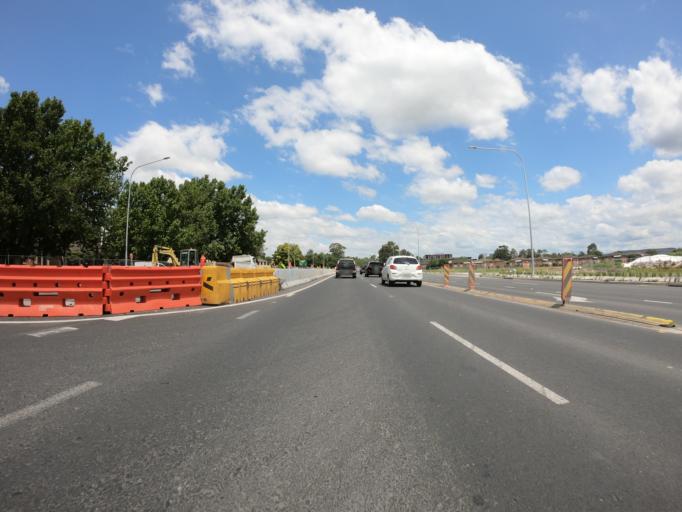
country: AU
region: New South Wales
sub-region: Penrith Municipality
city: Penrith
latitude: -33.7522
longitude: 150.6874
